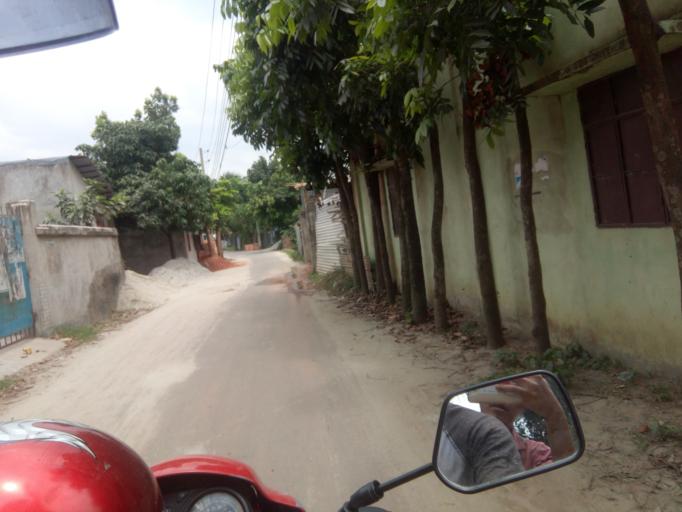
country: BD
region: Dhaka
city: Paltan
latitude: 23.7366
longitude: 90.4847
